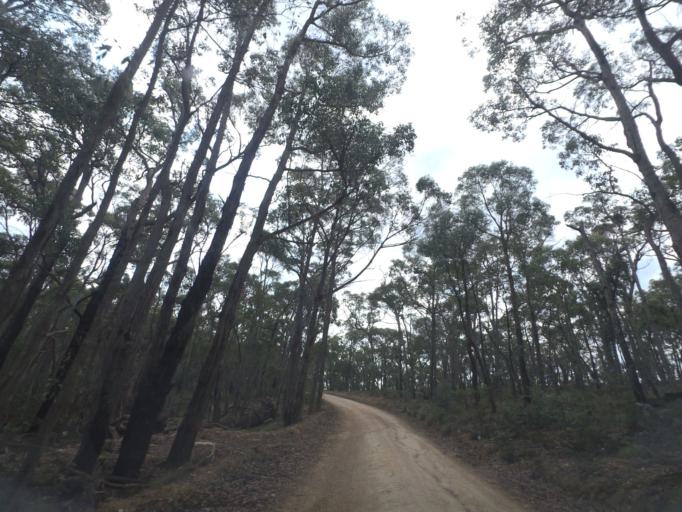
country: AU
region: Victoria
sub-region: Moorabool
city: Bacchus Marsh
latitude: -37.5128
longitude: 144.4334
